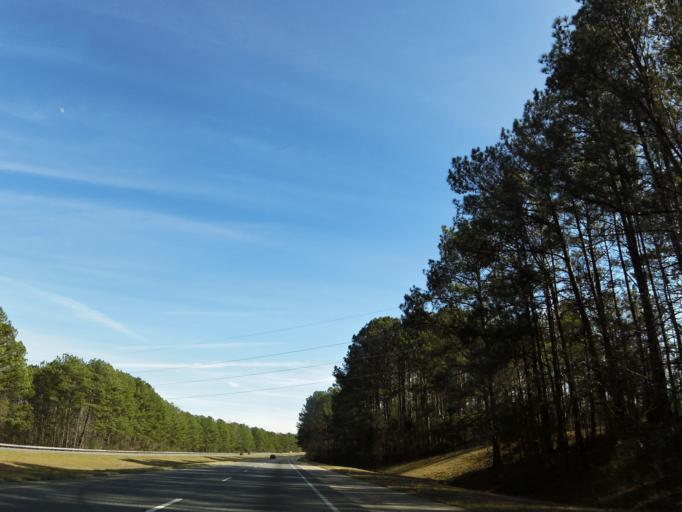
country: US
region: Georgia
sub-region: Harris County
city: Hamilton
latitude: 32.6967
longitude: -84.9996
